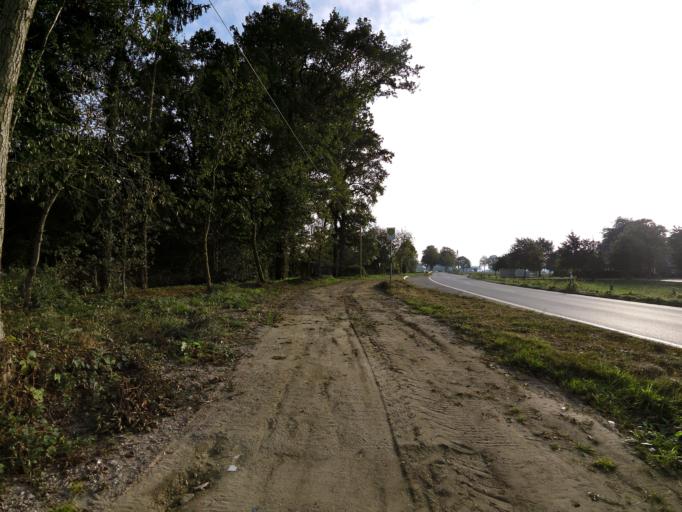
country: DE
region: North Rhine-Westphalia
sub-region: Regierungsbezirk Dusseldorf
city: Bocholt
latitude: 51.7966
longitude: 6.5587
